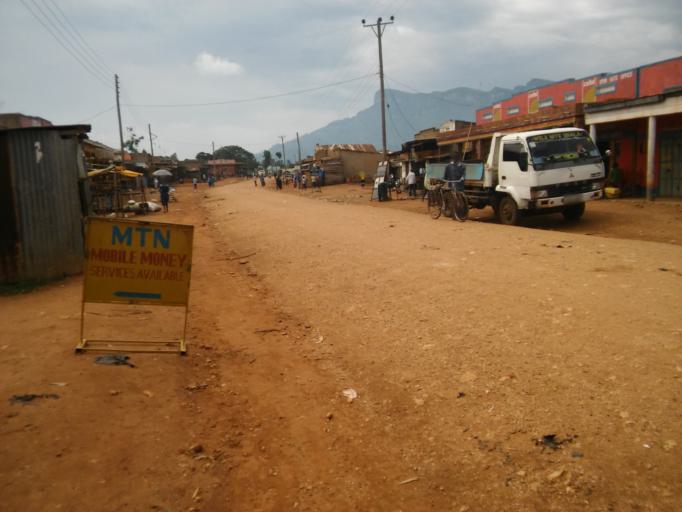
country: UG
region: Eastern Region
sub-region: Manafwa District
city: Manafwa
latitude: 0.8675
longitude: 34.3661
